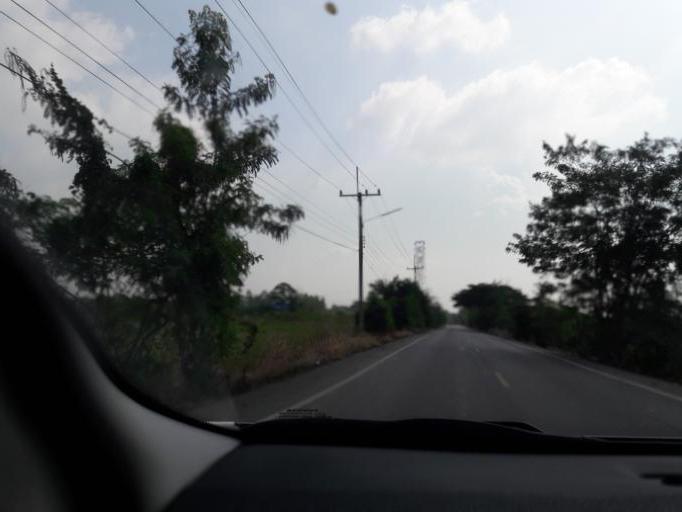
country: TH
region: Ang Thong
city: Ang Thong
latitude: 14.5780
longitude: 100.4278
